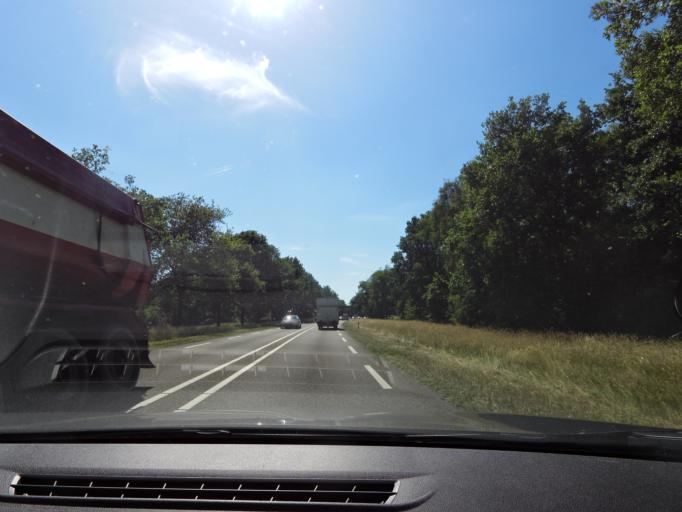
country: NL
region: Gelderland
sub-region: Oost Gelre
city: Lichtenvoorde
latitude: 52.0000
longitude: 6.5850
